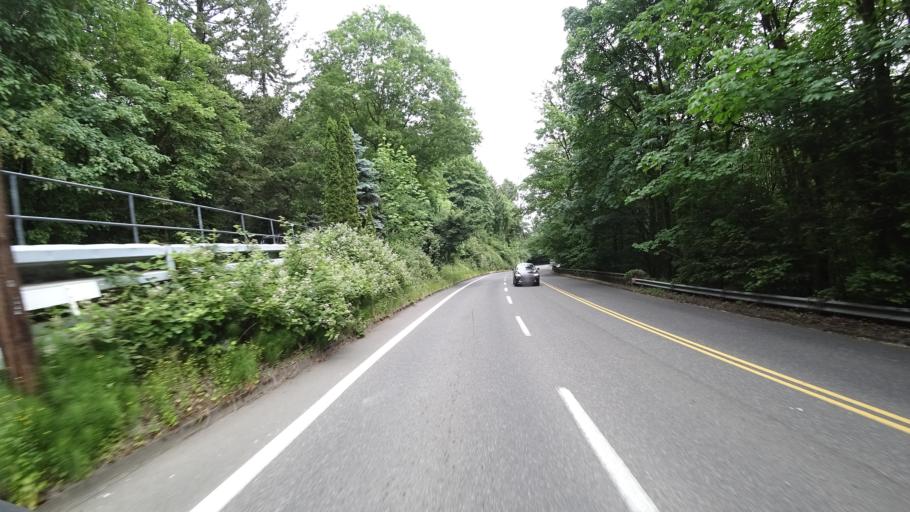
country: US
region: Oregon
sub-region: Multnomah County
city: Portland
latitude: 45.4804
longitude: -122.6857
